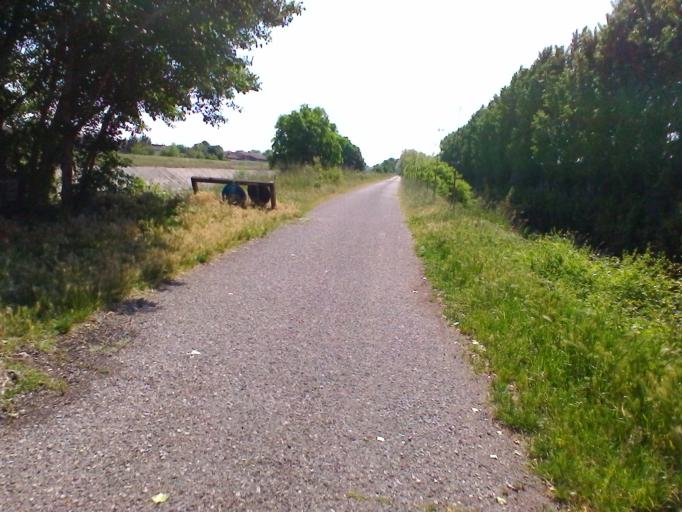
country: IT
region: Lombardy
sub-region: Provincia di Mantova
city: Soave
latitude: 45.1944
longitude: 10.7182
